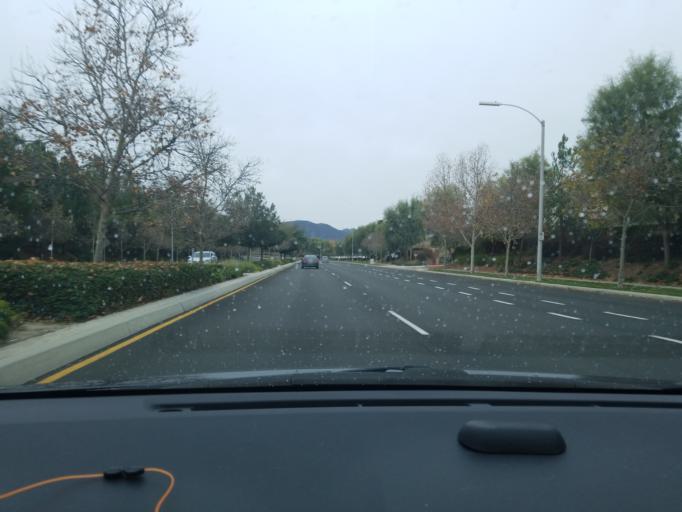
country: US
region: California
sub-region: Riverside County
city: Murrieta Hot Springs
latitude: 33.5403
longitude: -117.1613
